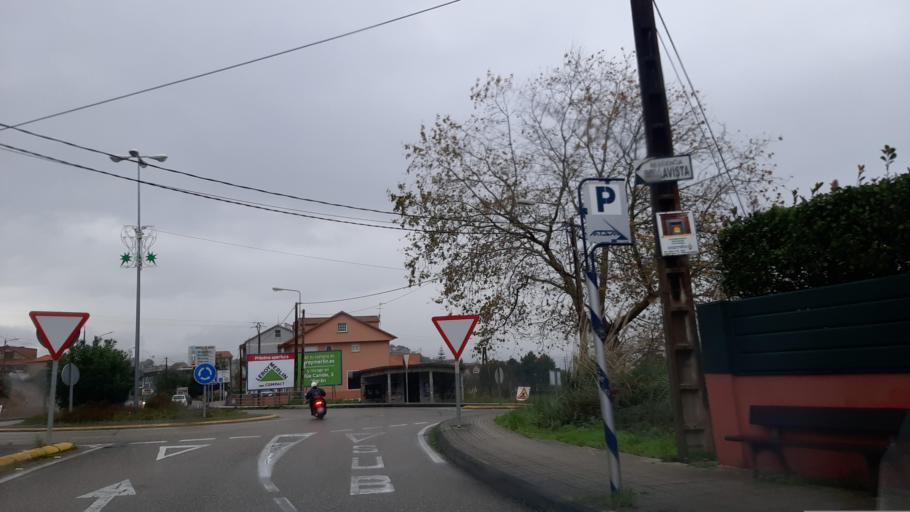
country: ES
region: Galicia
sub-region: Provincia de Pontevedra
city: Nigran
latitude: 42.1672
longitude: -8.8017
